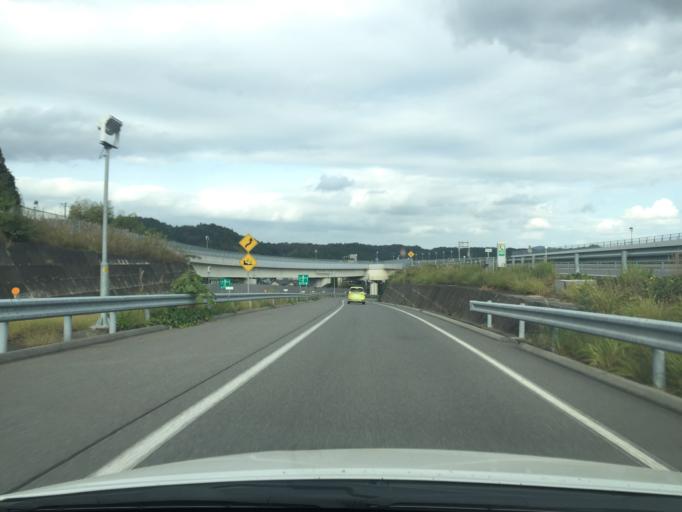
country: JP
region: Fukushima
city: Iwaki
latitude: 37.0657
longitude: 140.8361
